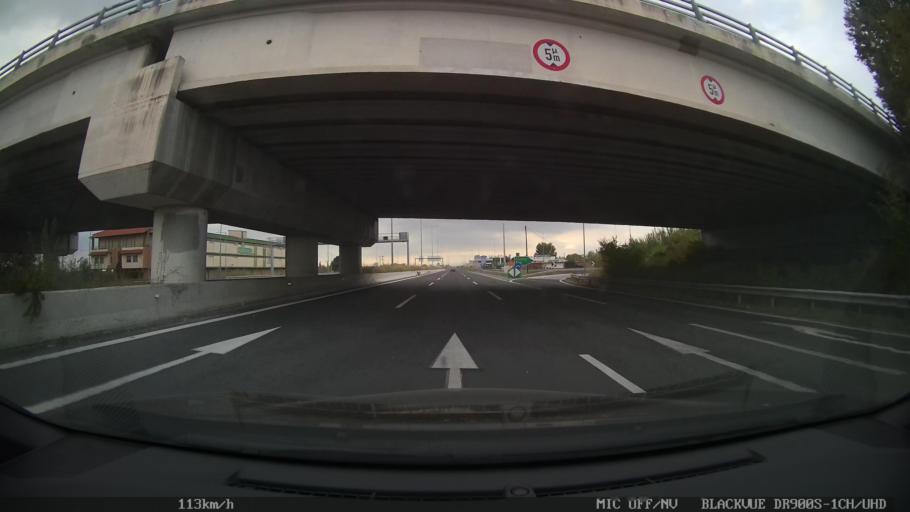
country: GR
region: Central Macedonia
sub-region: Nomos Pierias
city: Peristasi
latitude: 40.2558
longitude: 22.5315
